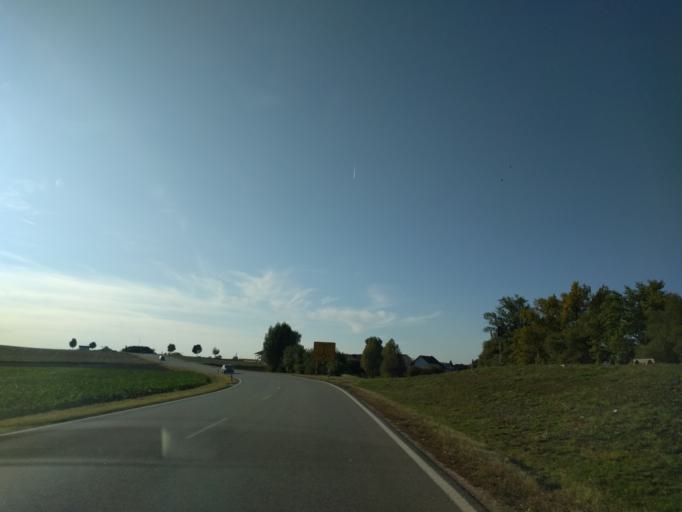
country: DE
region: Bavaria
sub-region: Lower Bavaria
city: Osterhofen
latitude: 48.7165
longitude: 13.0196
